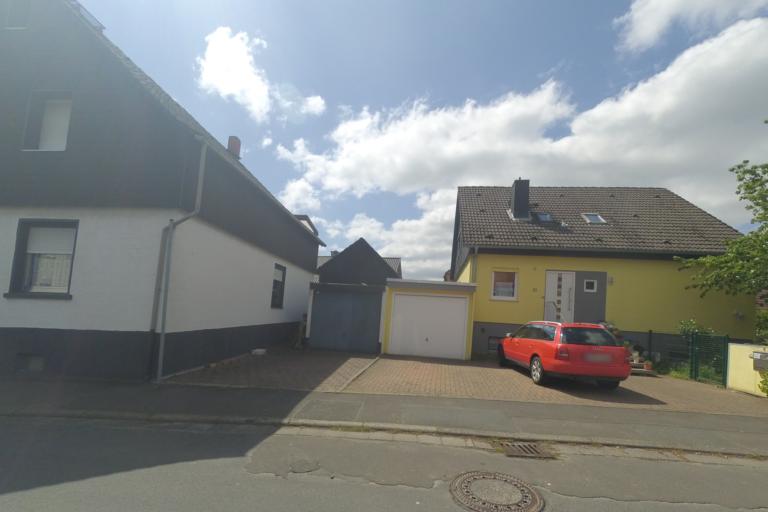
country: DE
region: Hesse
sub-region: Regierungsbezirk Darmstadt
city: Rosbach vor der Hohe
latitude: 50.2636
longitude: 8.7031
